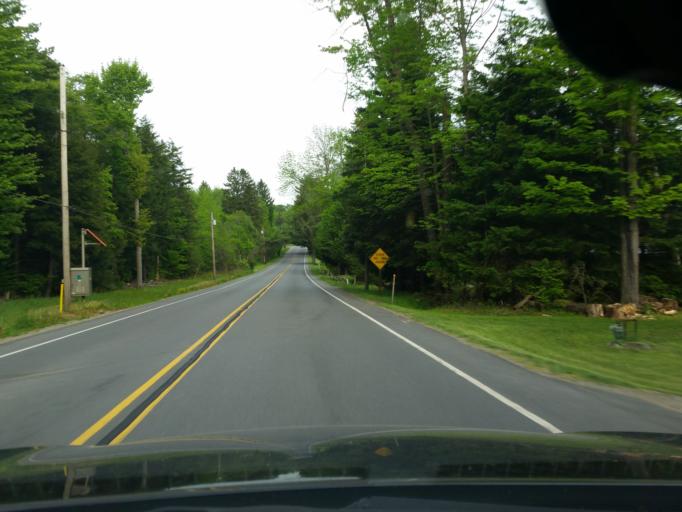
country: US
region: Pennsylvania
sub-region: McKean County
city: Kane
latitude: 41.5730
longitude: -78.9130
